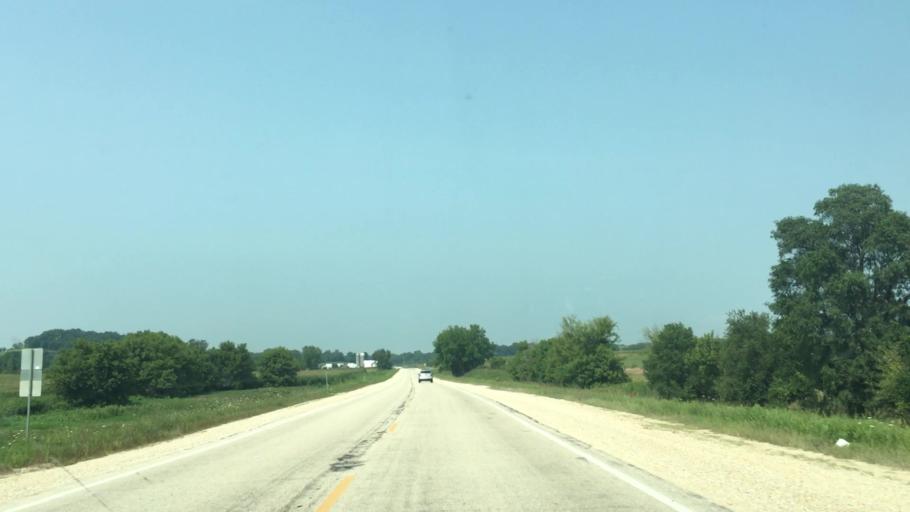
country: US
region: Iowa
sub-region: Fayette County
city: West Union
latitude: 43.0540
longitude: -91.8392
